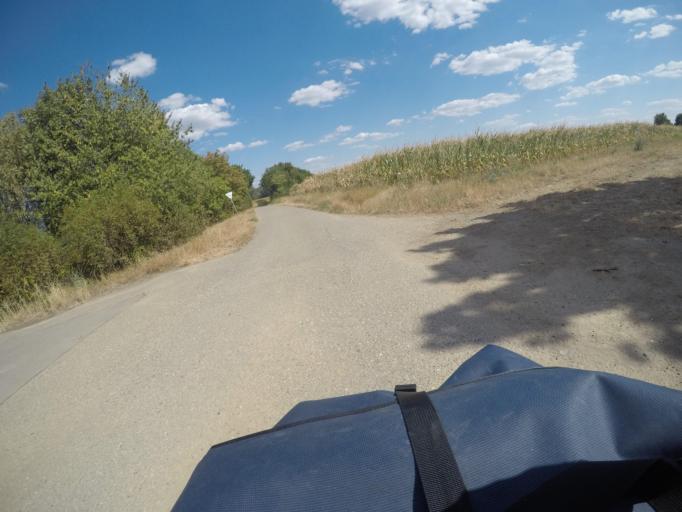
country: DE
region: Rheinland-Pfalz
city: Gartenstadt
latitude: 49.4790
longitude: 8.3869
